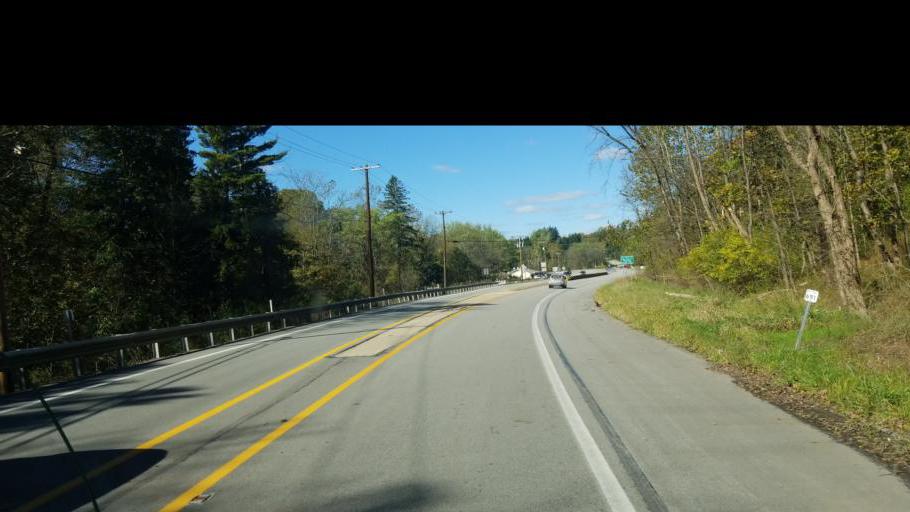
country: US
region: Pennsylvania
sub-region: Westmoreland County
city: Ligonier
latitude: 40.2337
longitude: -79.2273
